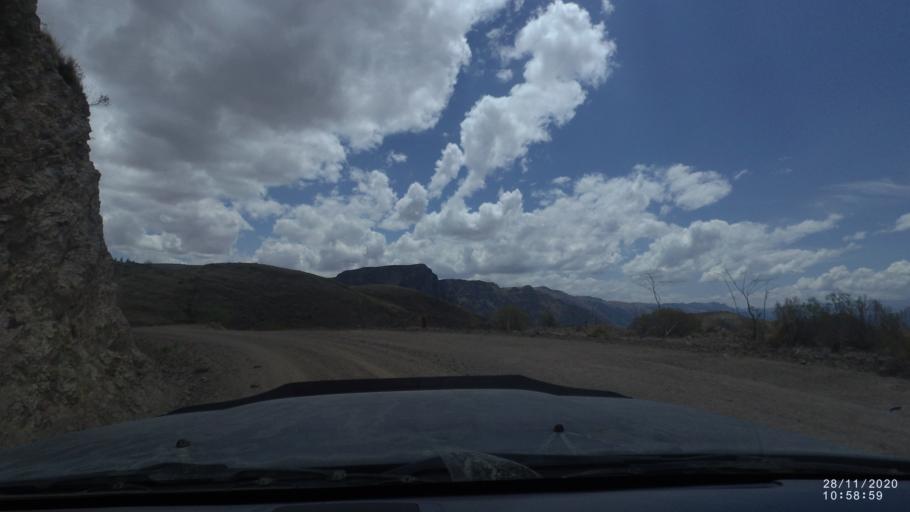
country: BO
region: Cochabamba
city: Capinota
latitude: -17.7754
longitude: -66.1086
